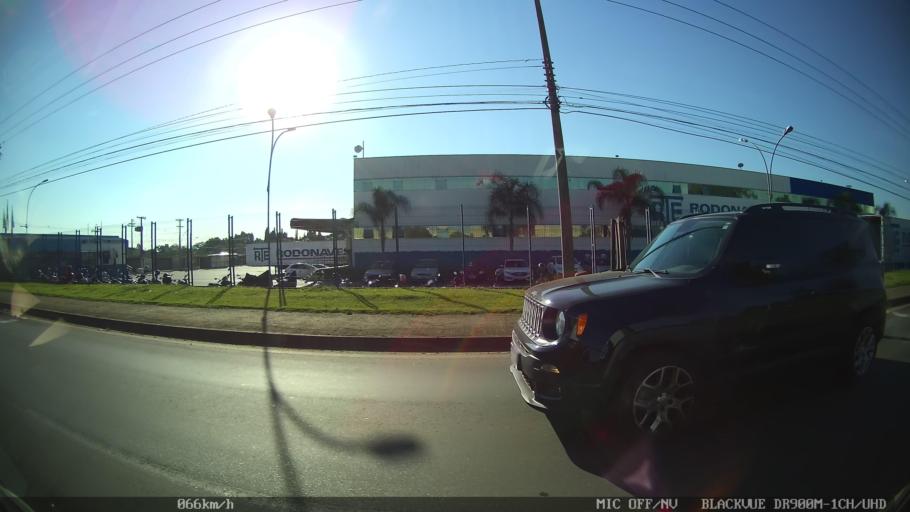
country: BR
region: Sao Paulo
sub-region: Nova Odessa
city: Nova Odessa
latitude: -22.7645
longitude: -47.2584
